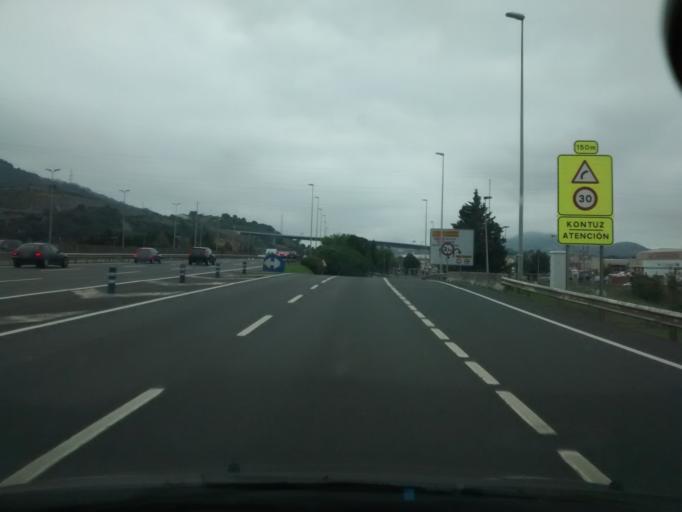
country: ES
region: Basque Country
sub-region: Bizkaia
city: Barakaldo
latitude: 43.2903
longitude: -3.0080
